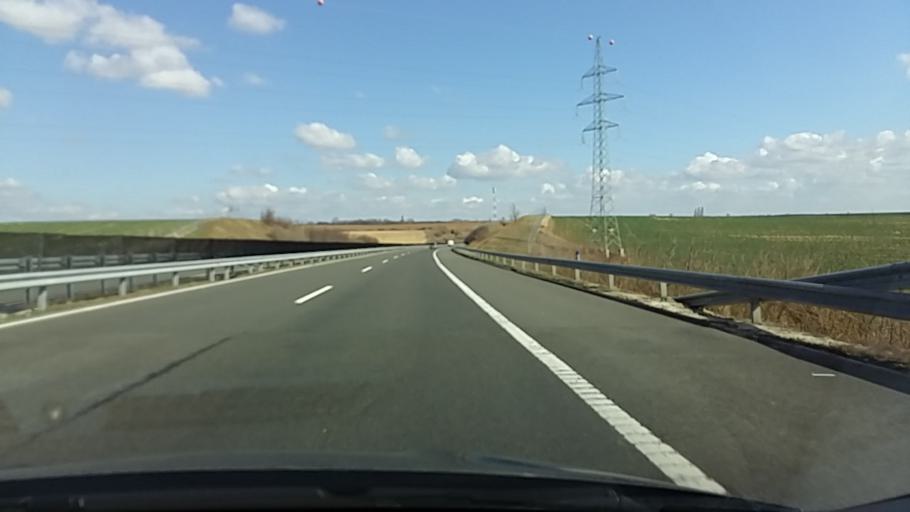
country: HU
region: Baranya
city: Kozarmisleny
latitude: 46.0258
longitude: 18.3222
